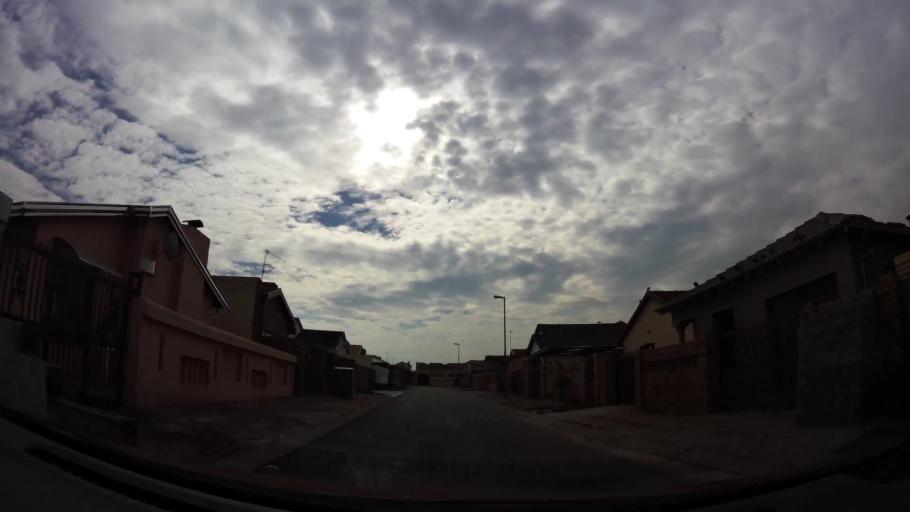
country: ZA
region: Gauteng
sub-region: City of Johannesburg Metropolitan Municipality
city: Soweto
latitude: -26.2720
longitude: 27.8291
